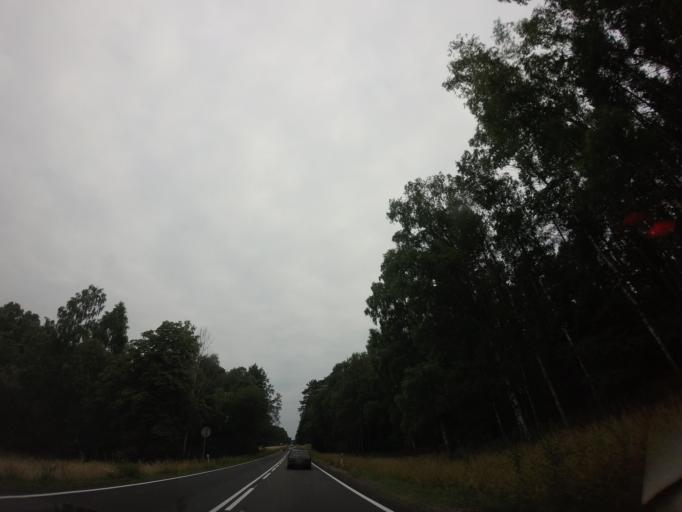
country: PL
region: West Pomeranian Voivodeship
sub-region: Powiat walecki
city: Miroslawiec
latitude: 53.3292
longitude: 16.0194
